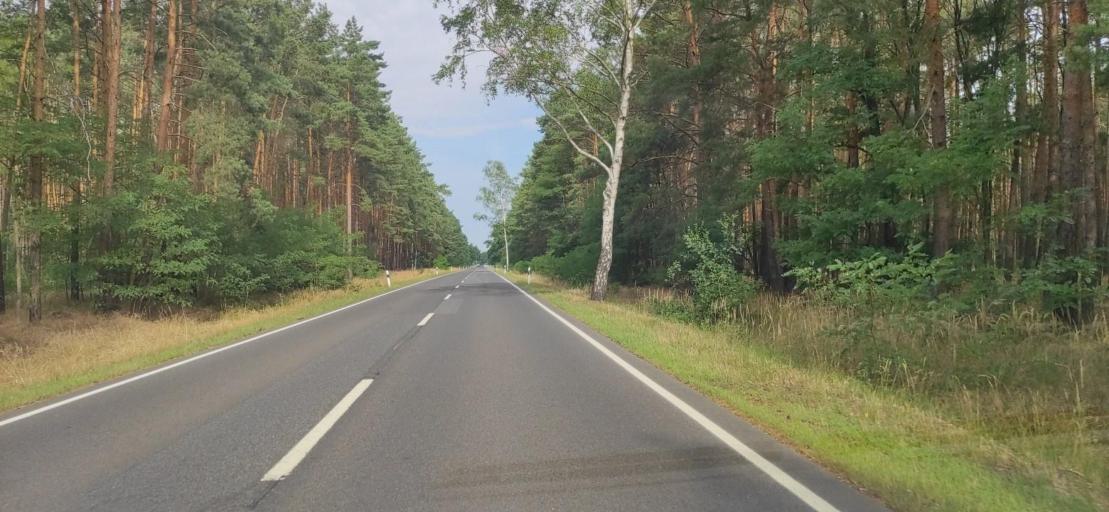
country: DE
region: Brandenburg
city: Forst
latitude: 51.6971
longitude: 14.7034
